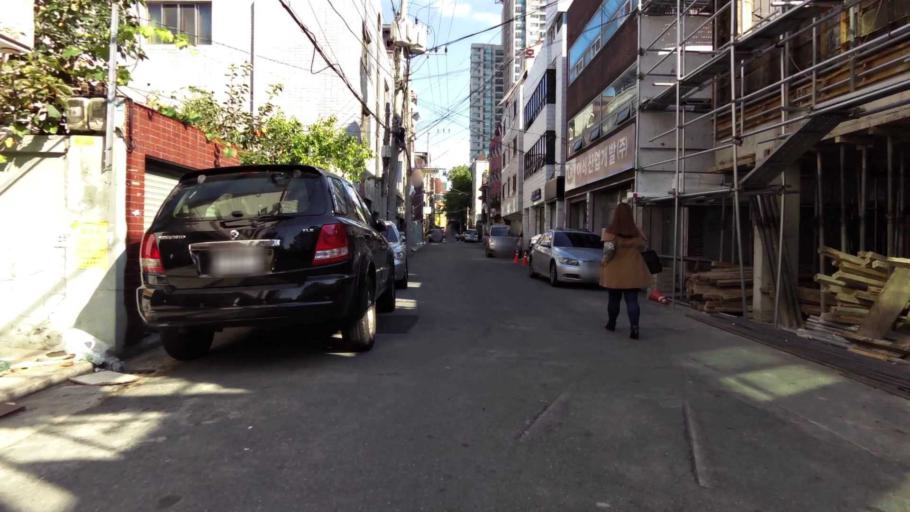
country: KR
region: Daegu
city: Daegu
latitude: 35.8596
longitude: 128.6431
